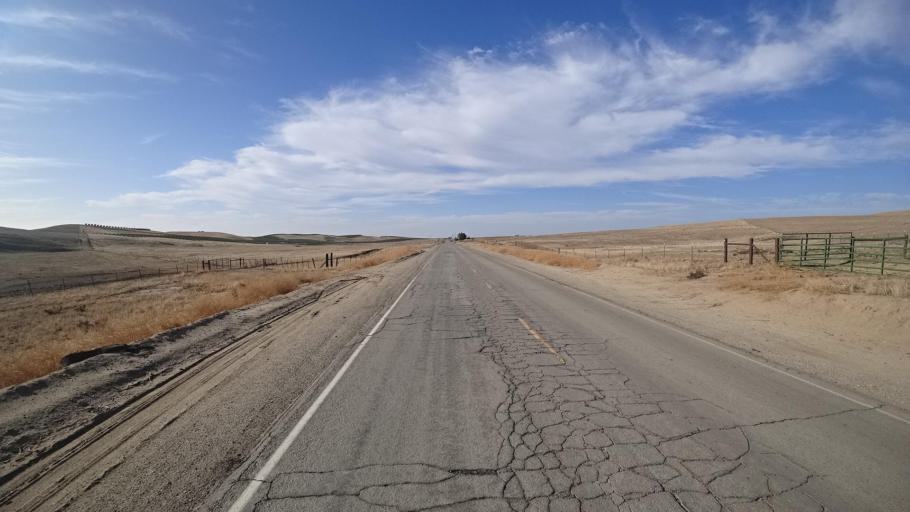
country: US
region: California
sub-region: Kern County
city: McFarland
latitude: 35.6081
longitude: -119.0630
